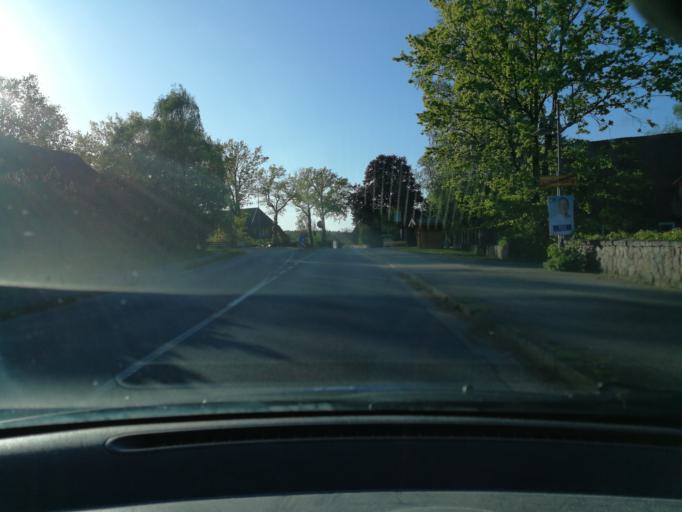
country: DE
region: Lower Saxony
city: Betzendorf
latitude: 53.1513
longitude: 10.2957
